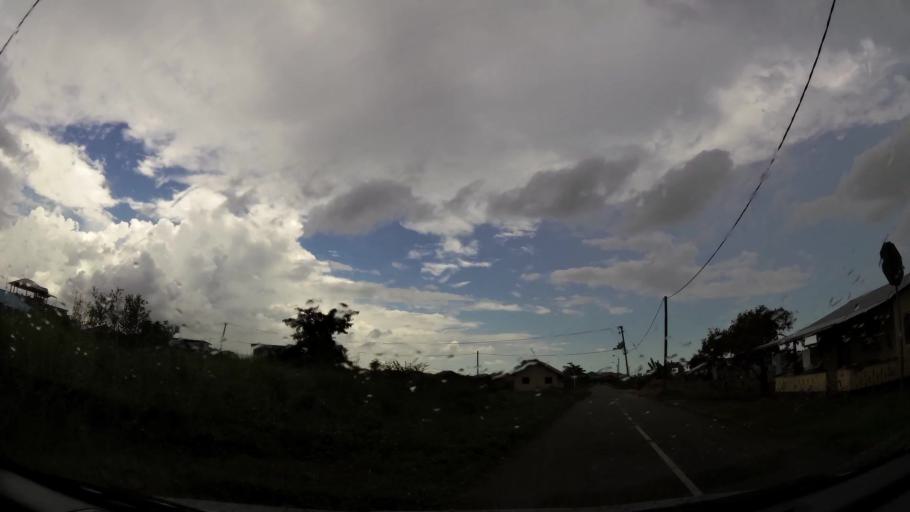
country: SR
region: Commewijne
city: Nieuw Amsterdam
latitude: 5.8536
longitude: -55.1129
